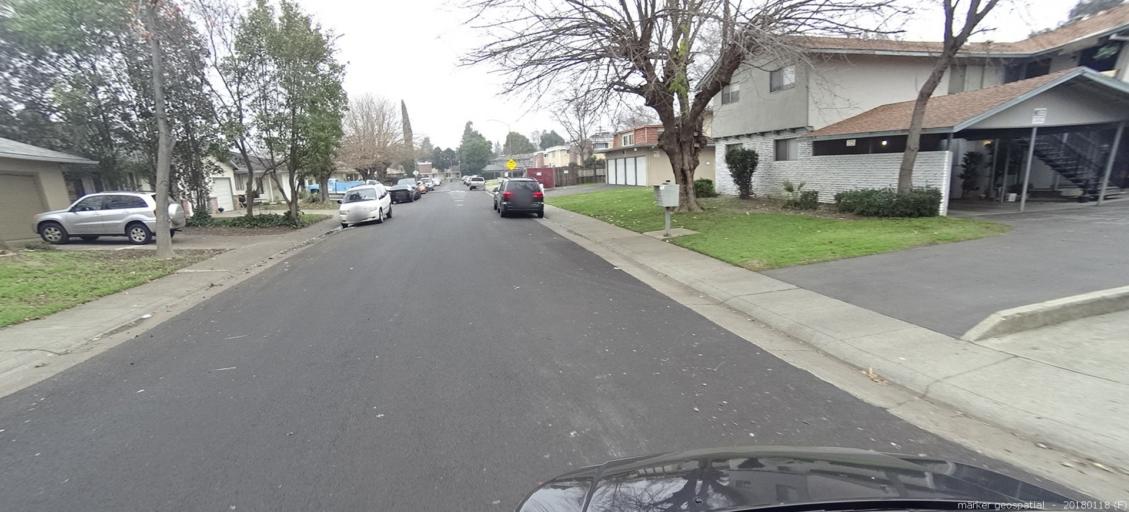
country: US
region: California
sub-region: Sacramento County
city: Rancho Cordova
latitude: 38.5841
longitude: -121.3157
